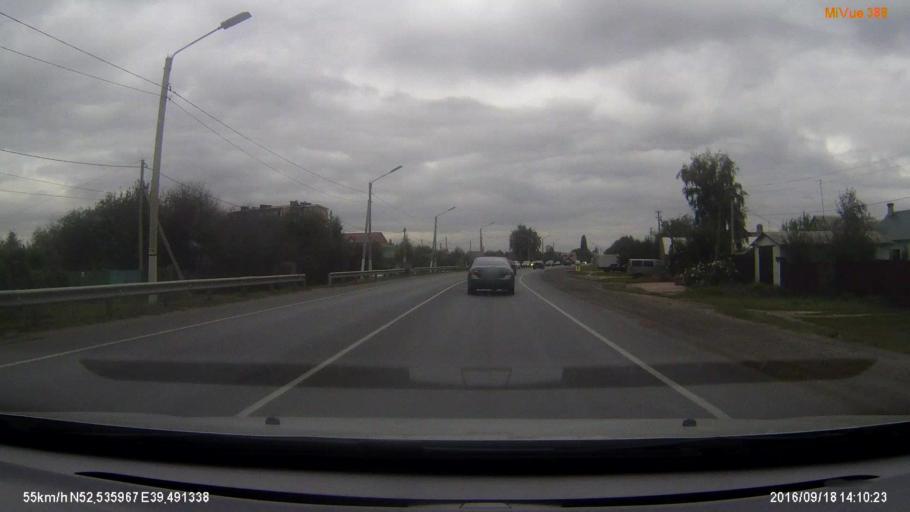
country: RU
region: Lipetsk
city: Syrskoye
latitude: 52.5943
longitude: 39.5186
